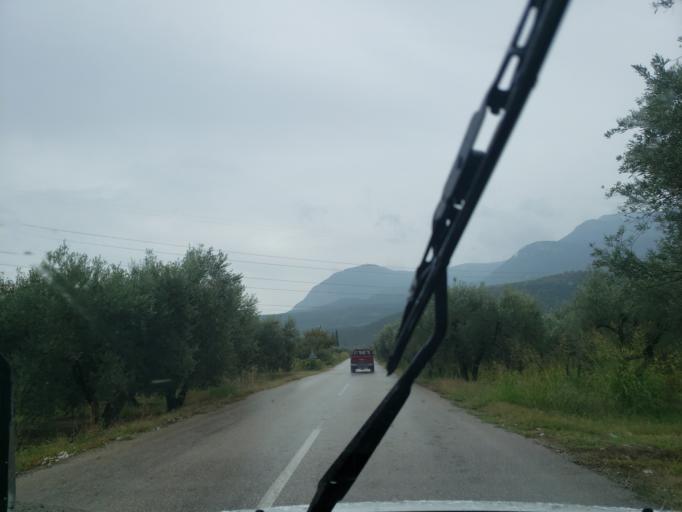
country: GR
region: Central Greece
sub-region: Nomos Fthiotidos
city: Anthili
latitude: 38.8019
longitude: 22.4610
